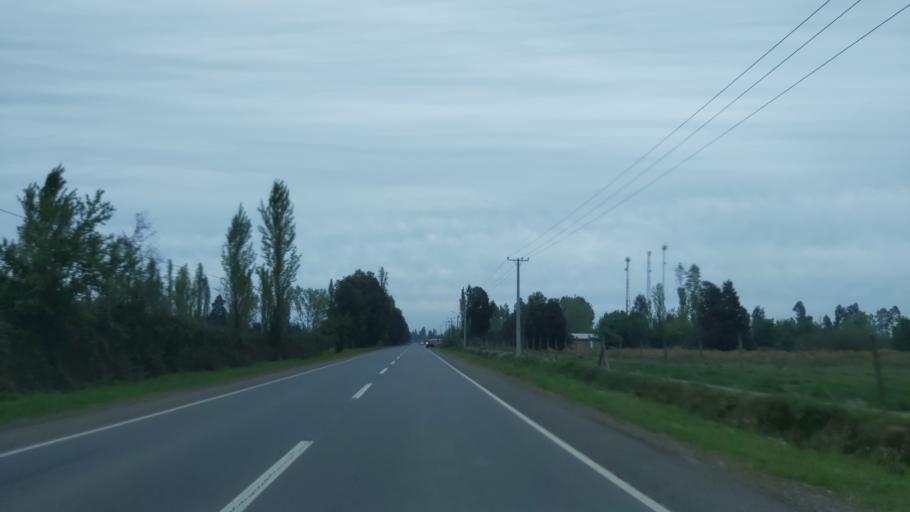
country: CL
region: Maule
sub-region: Provincia de Linares
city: Colbun
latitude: -35.7271
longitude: -71.4866
